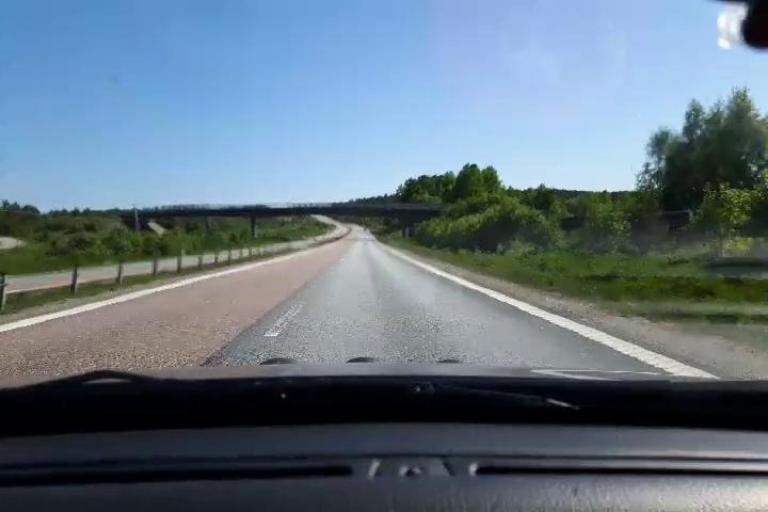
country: SE
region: Gaevleborg
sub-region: Soderhamns Kommun
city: Soderhamn
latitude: 61.3589
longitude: 17.0145
